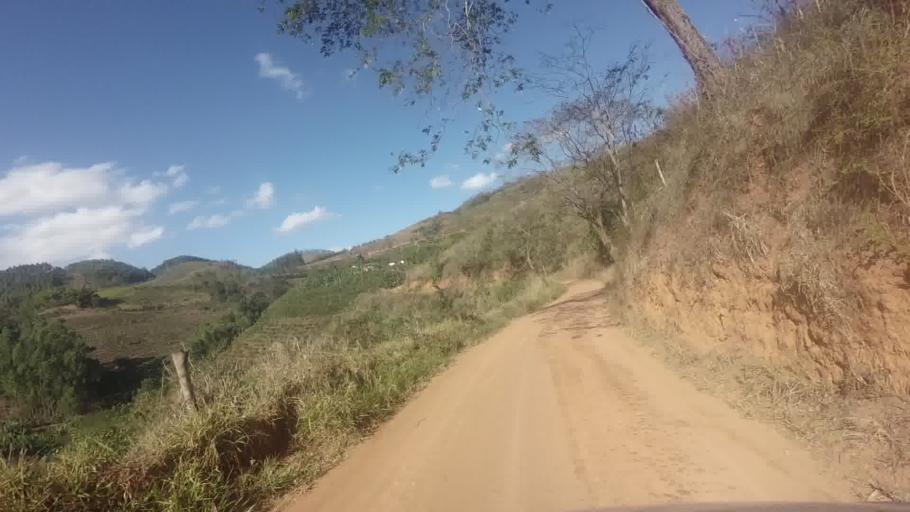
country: BR
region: Espirito Santo
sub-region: Sao Jose Do Calcado
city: Sao Jose do Calcado
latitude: -21.0288
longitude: -41.5819
